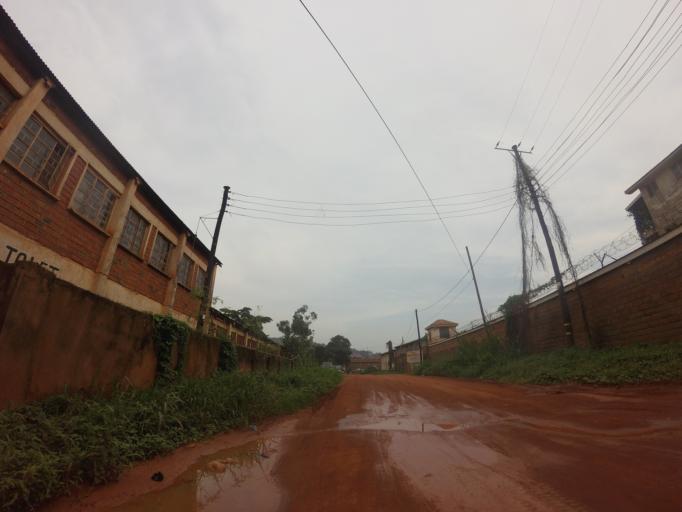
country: UG
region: Central Region
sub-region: Wakiso District
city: Kireka
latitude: 0.3404
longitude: 32.6227
